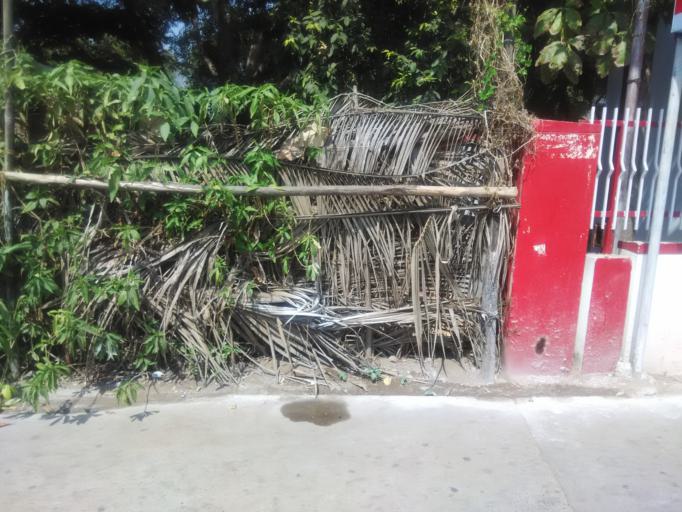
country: IN
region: Andhra Pradesh
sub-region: Prakasam
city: Chirala
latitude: 15.8270
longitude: 80.3511
